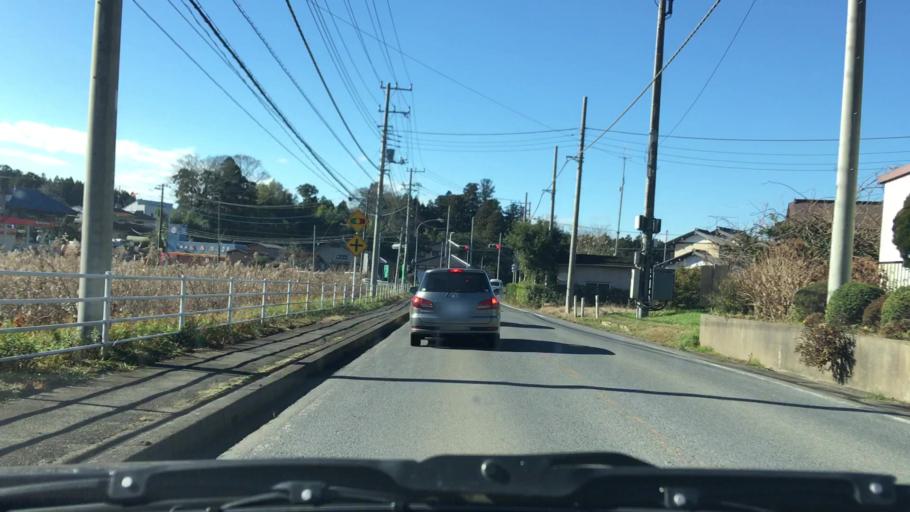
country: JP
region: Chiba
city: Sawara
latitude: 35.8169
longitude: 140.5297
